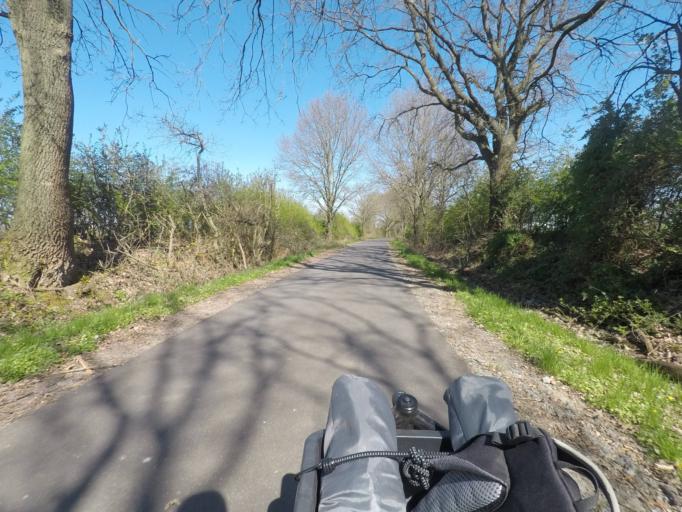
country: DE
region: Schleswig-Holstein
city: Braak
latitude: 53.6041
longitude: 10.2782
